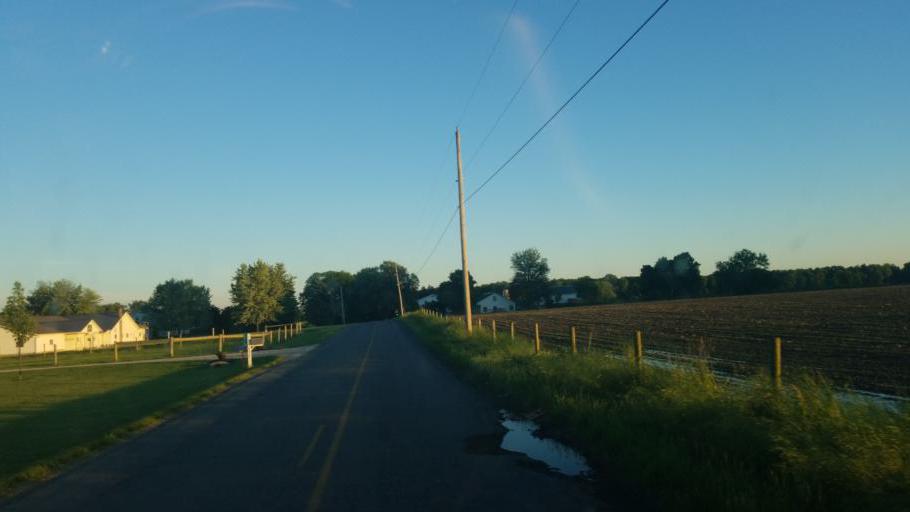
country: US
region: Indiana
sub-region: Elkhart County
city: Nappanee
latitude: 41.4373
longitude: -86.0304
